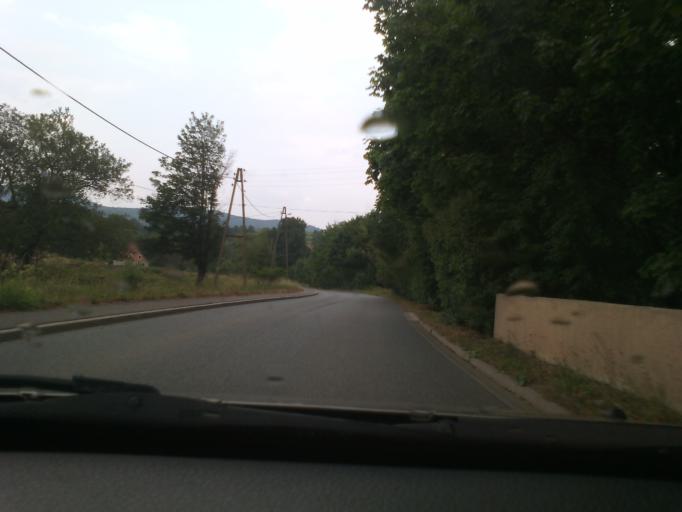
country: PL
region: Lower Silesian Voivodeship
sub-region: Powiat walbrzyski
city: Walbrzych
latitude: 50.6974
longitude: 16.2733
